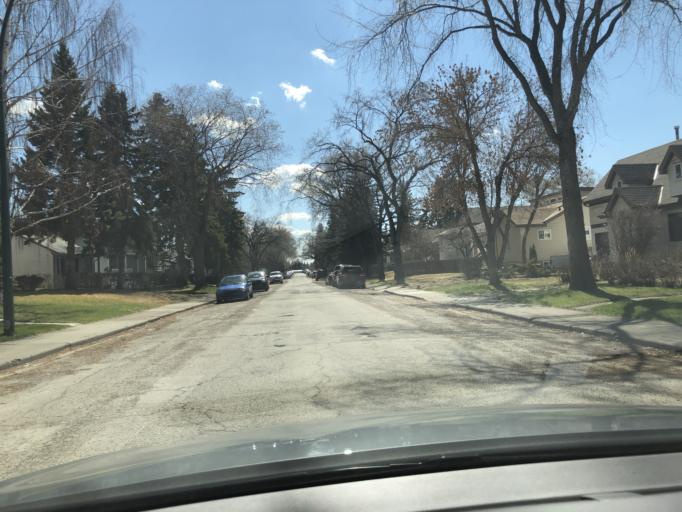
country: CA
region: Alberta
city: Calgary
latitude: 50.9971
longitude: -114.0149
